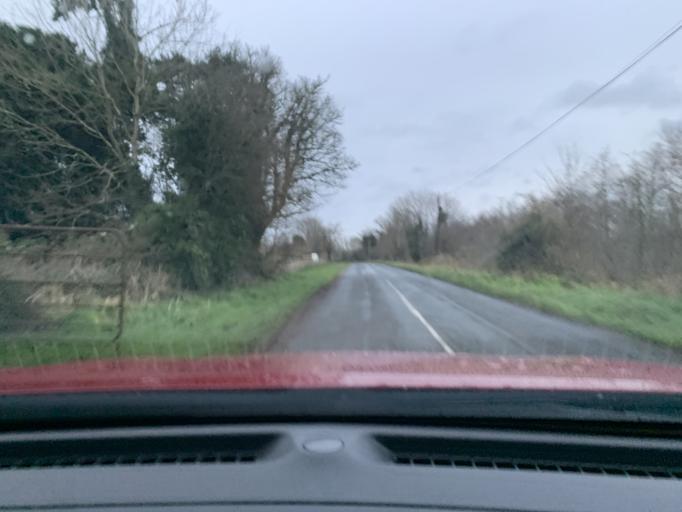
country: IE
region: Connaught
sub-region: Roscommon
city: Boyle
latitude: 54.0408
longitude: -8.3337
